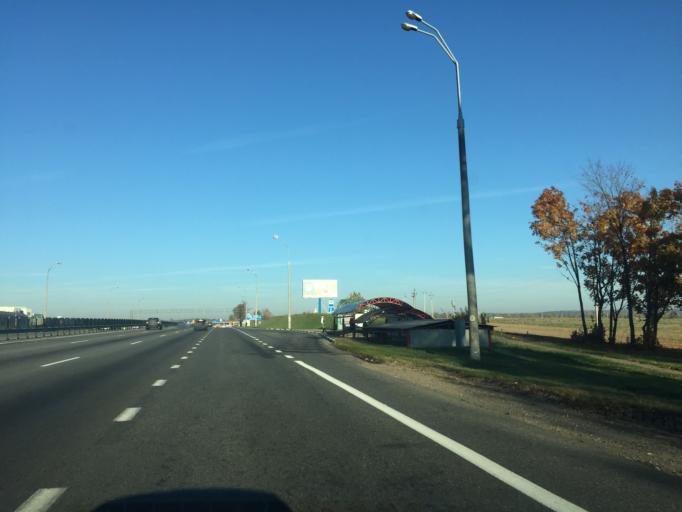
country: BY
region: Minsk
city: Pryvol'ny
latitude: 53.8006
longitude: 27.8028
